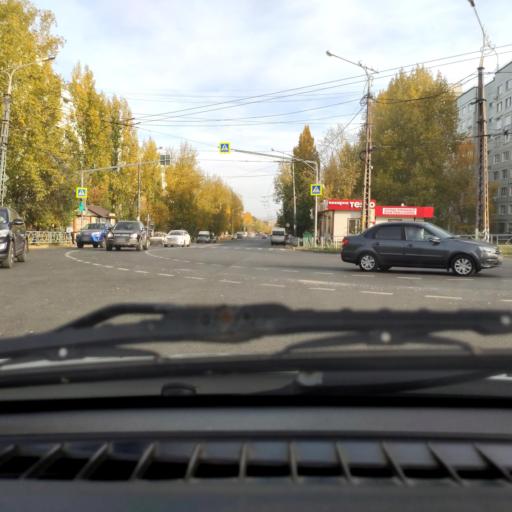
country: RU
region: Samara
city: Zhigulevsk
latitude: 53.4829
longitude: 49.4600
